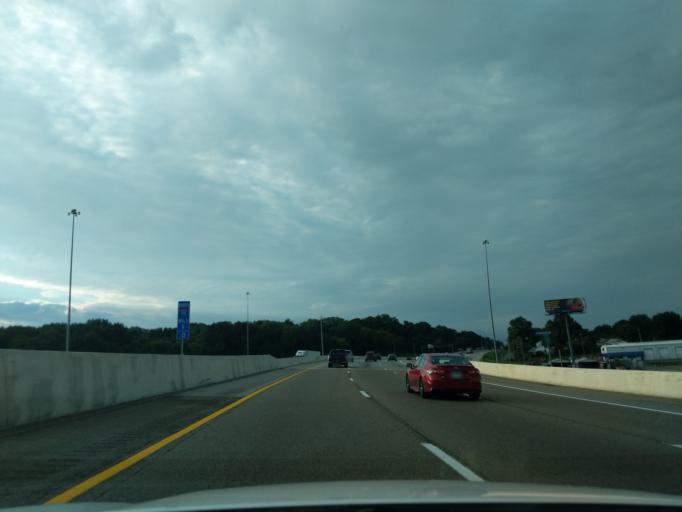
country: US
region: Tennessee
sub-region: Shelby County
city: New South Memphis
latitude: 35.0861
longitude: -90.0761
